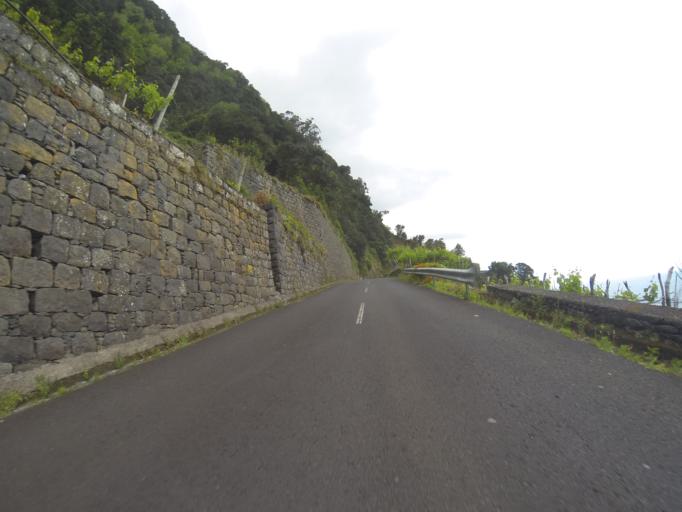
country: PT
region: Madeira
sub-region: Sao Vicente
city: Sao Vicente
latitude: 32.8185
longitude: -17.1022
